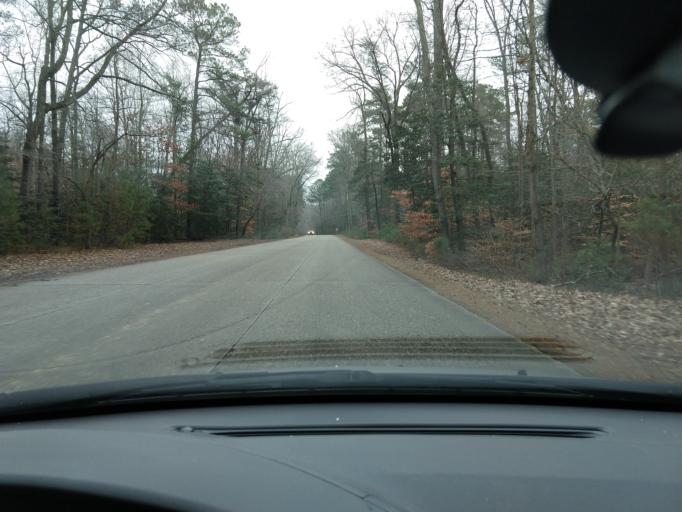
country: US
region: Virginia
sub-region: City of Williamsburg
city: Williamsburg
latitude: 37.2825
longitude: -76.6348
